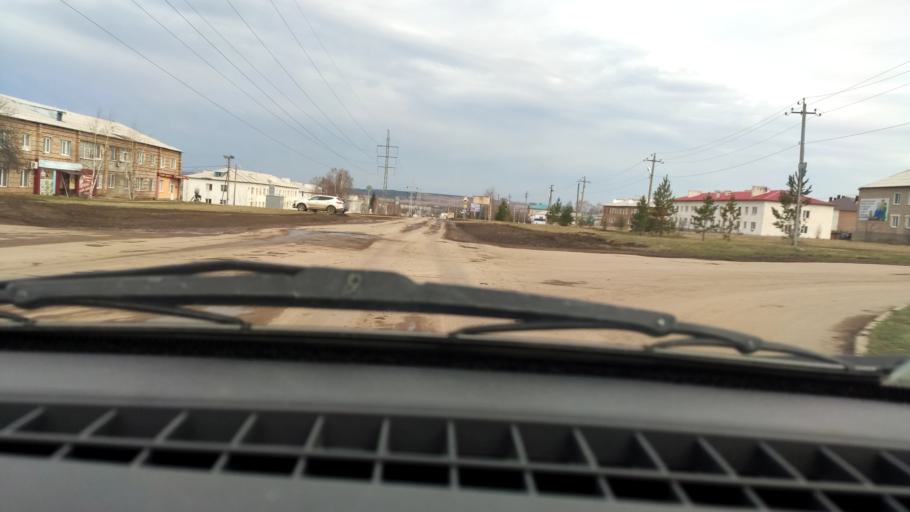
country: RU
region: Bashkortostan
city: Davlekanovo
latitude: 54.2270
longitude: 55.0364
